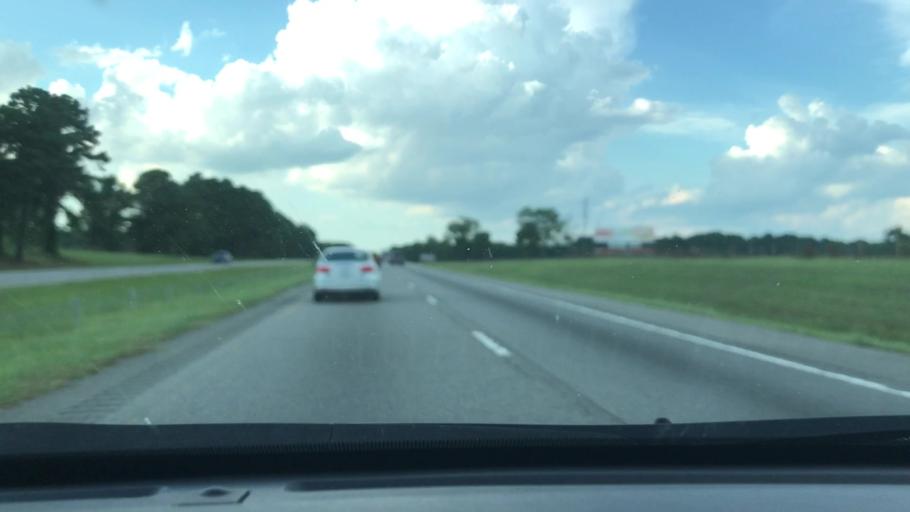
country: US
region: North Carolina
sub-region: Robeson County
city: Saint Pauls
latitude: 34.8638
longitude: -78.9648
